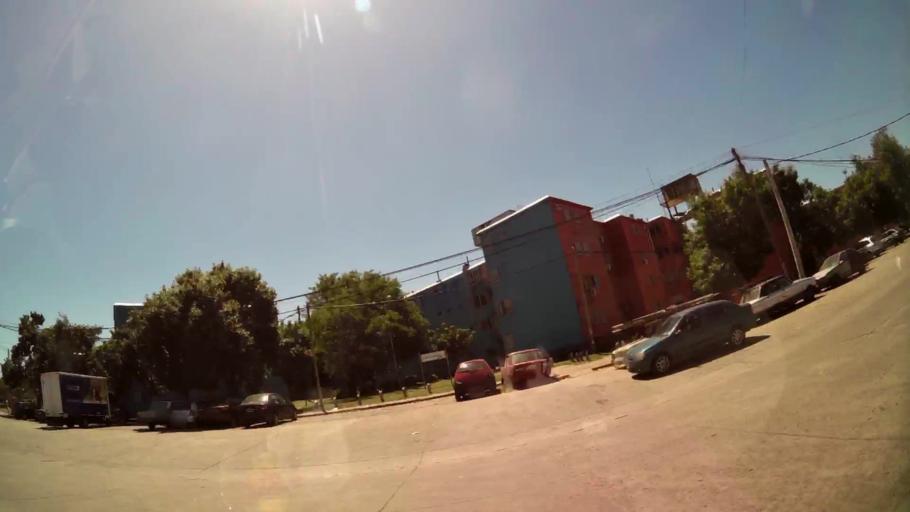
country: AR
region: Buenos Aires
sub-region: Partido de Tigre
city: Tigre
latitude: -34.4848
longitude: -58.6538
